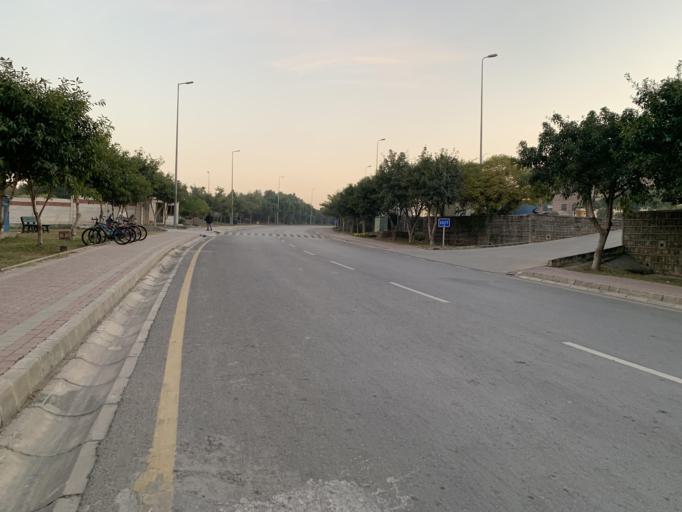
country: PK
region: Punjab
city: Rawalpindi
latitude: 33.6444
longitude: 72.9941
